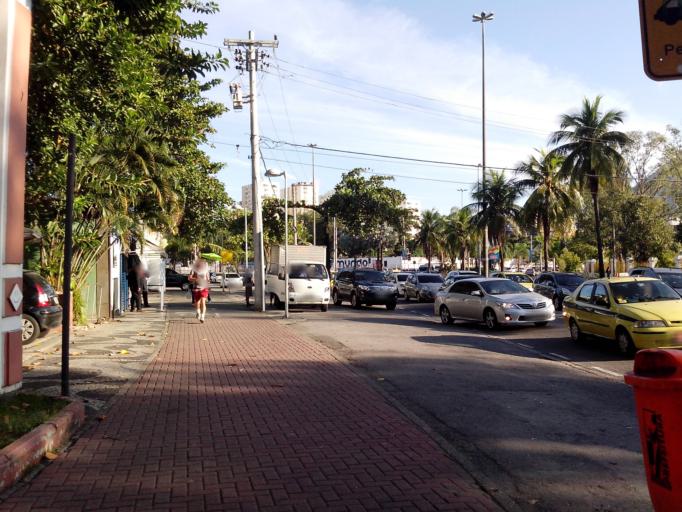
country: BR
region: Rio de Janeiro
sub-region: Rio De Janeiro
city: Rio de Janeiro
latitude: -22.9758
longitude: -43.2186
